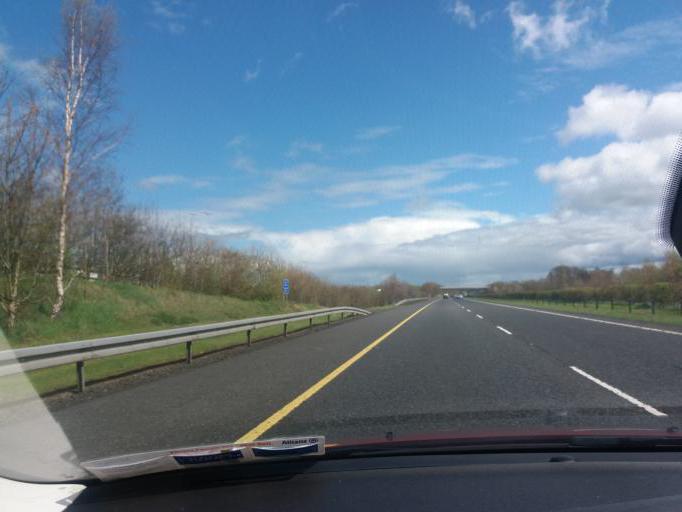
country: IE
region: Leinster
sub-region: Laois
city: Portarlington
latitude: 53.1054
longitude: -7.1376
